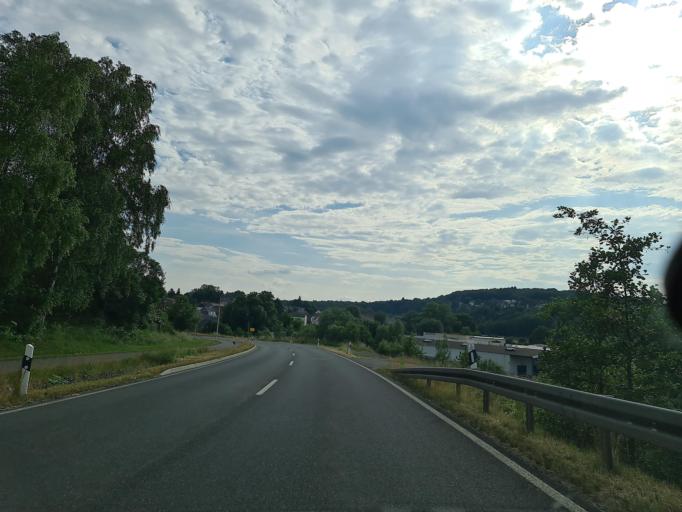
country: DE
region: Saxony
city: Plauen
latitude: 50.5134
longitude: 12.1675
